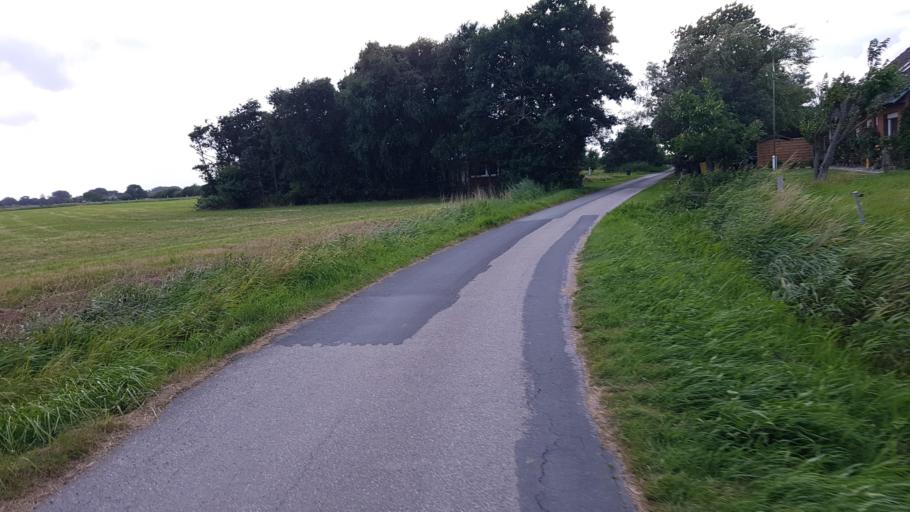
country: DE
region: Schleswig-Holstein
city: Tating
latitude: 54.2848
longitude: 8.6912
